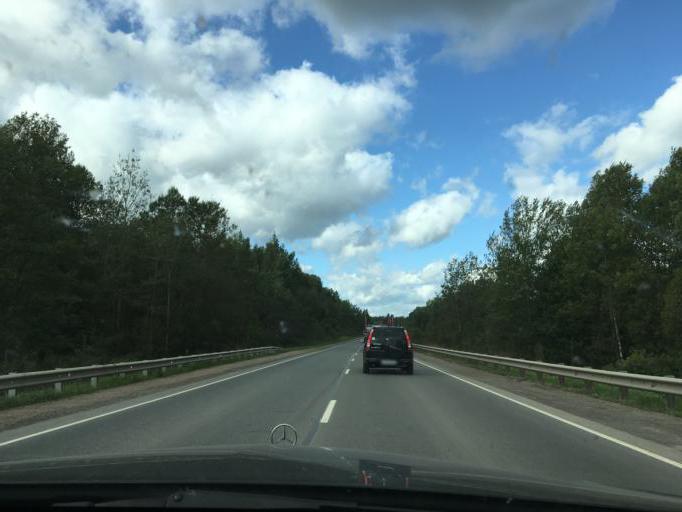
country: RU
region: Pskov
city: Novosokol'niki
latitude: 56.3021
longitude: 30.2107
